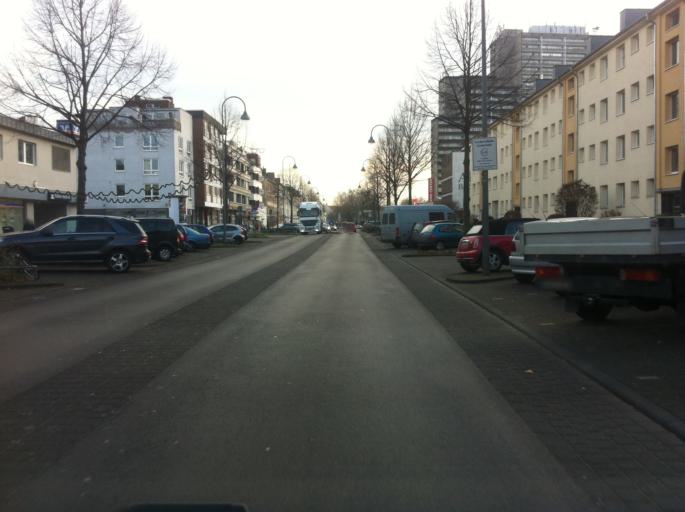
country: DE
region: North Rhine-Westphalia
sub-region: Regierungsbezirk Koln
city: Bilderstoeckchen
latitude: 50.9591
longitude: 6.8972
